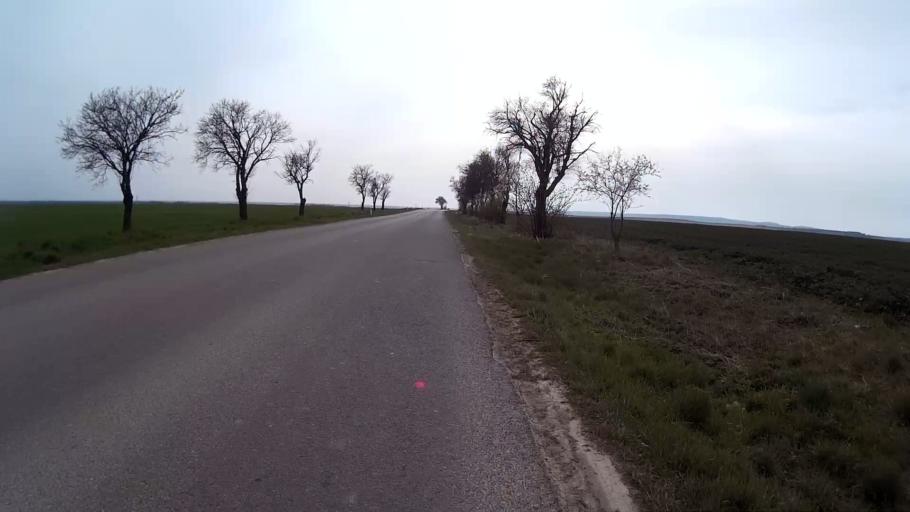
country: CZ
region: South Moravian
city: Orechov
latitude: 49.0724
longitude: 16.5327
